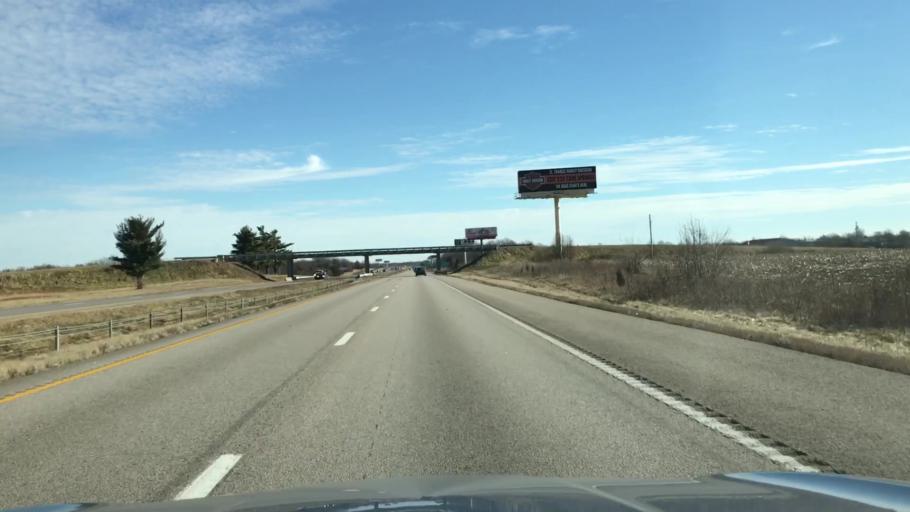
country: US
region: Missouri
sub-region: Gasconade County
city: Hermann
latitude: 38.8680
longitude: -91.3323
